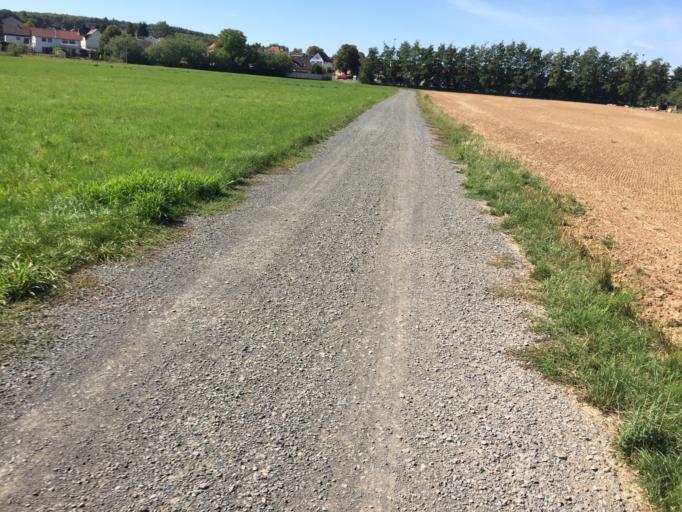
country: DE
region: Hesse
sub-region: Regierungsbezirk Giessen
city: Reiskirchen
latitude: 50.5920
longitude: 8.8620
